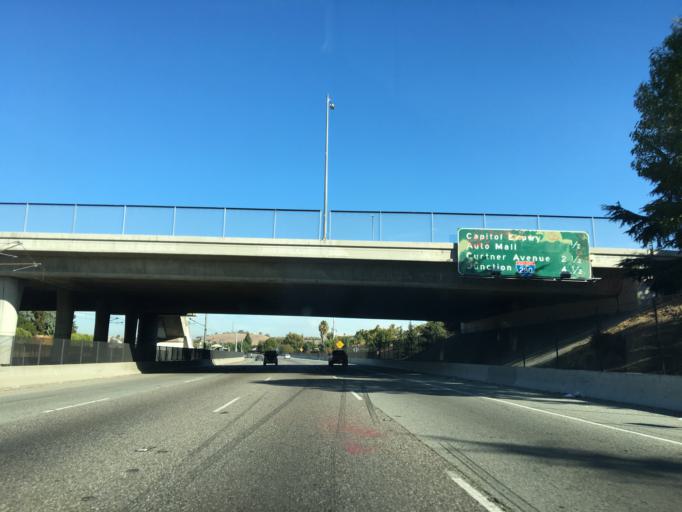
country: US
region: California
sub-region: Santa Clara County
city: Seven Trees
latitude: 37.2655
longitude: -121.8588
